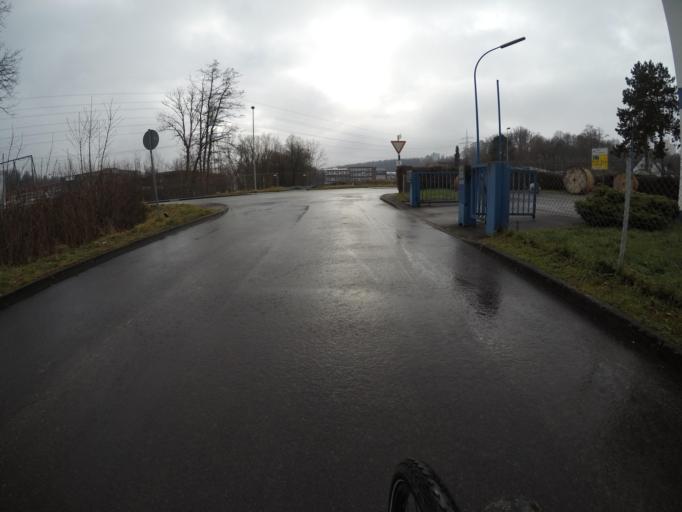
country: DE
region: Baden-Wuerttemberg
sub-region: Regierungsbezirk Stuttgart
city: Nurtingen
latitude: 48.6094
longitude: 9.3475
